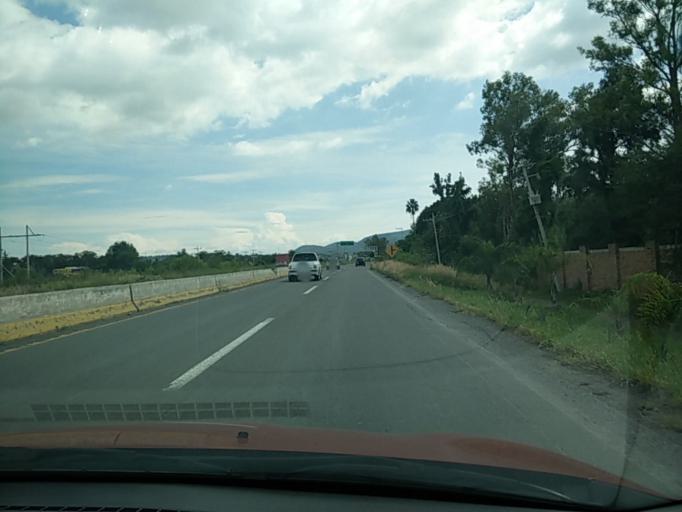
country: MX
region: Jalisco
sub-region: Ixtlahuacan de los Membrillos
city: Los Cedros
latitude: 20.4009
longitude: -103.2274
